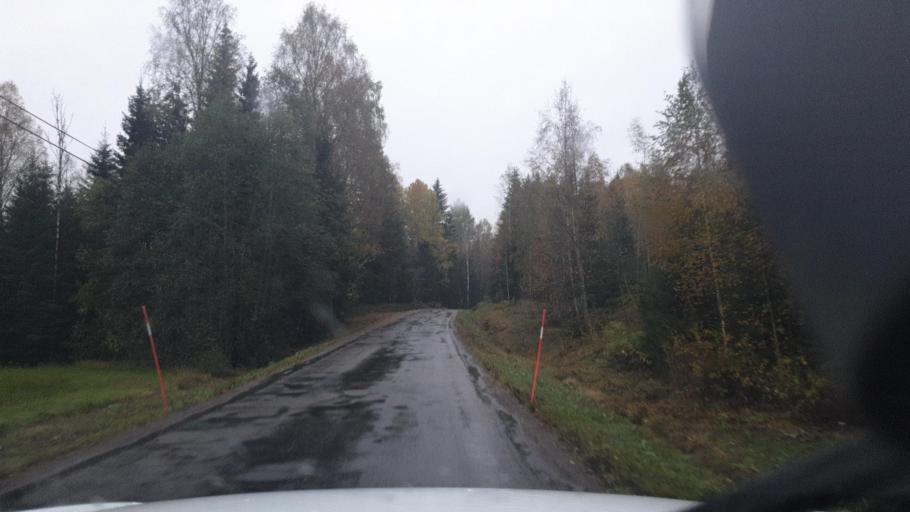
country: SE
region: Vaermland
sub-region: Eda Kommun
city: Amotfors
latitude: 59.8662
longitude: 12.4275
